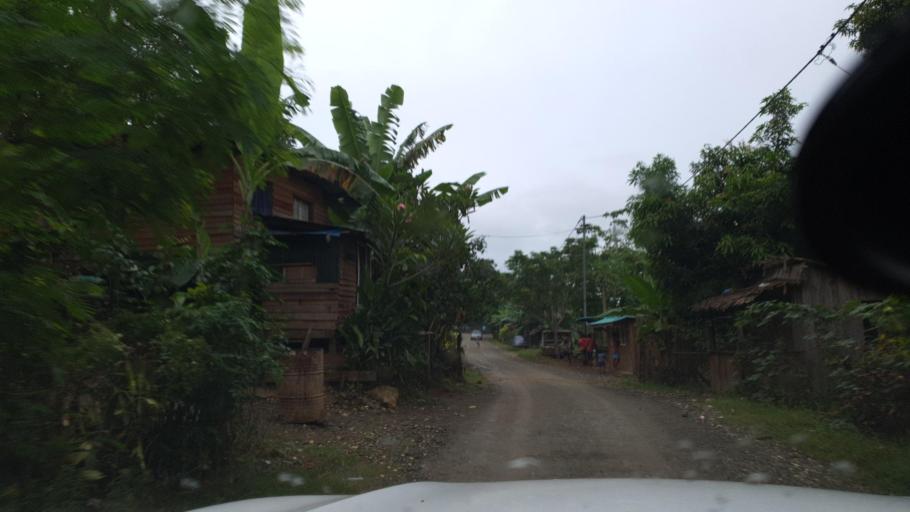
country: SB
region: Guadalcanal
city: Honiara
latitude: -9.4524
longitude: 159.9859
